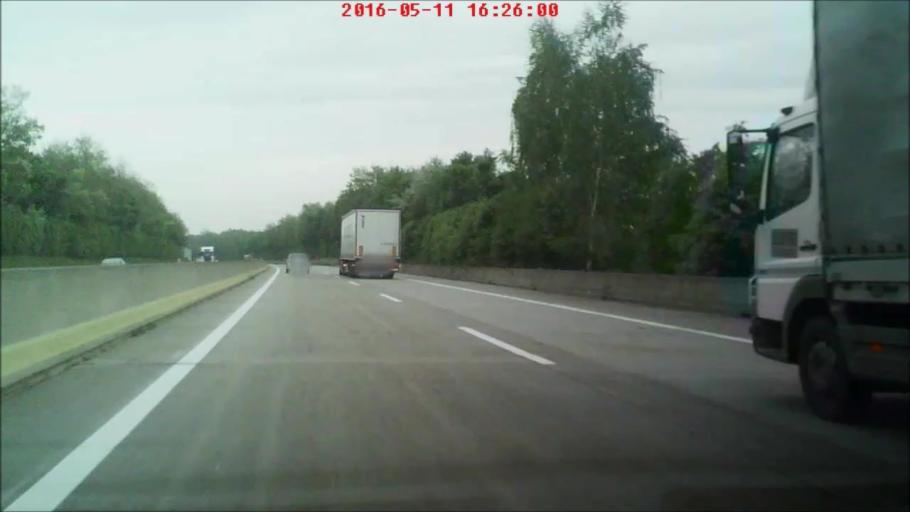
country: AT
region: Styria
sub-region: Politischer Bezirk Leibnitz
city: Sankt Veit am Vogau
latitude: 46.7411
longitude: 15.6164
